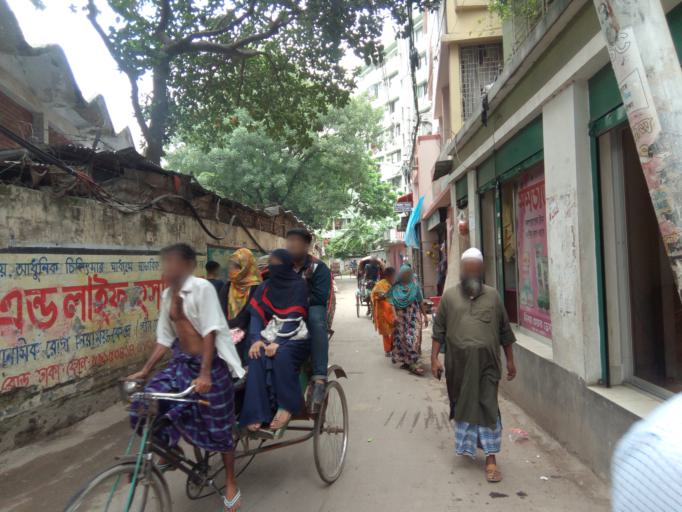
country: BD
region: Dhaka
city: Azimpur
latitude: 23.7523
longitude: 90.3898
